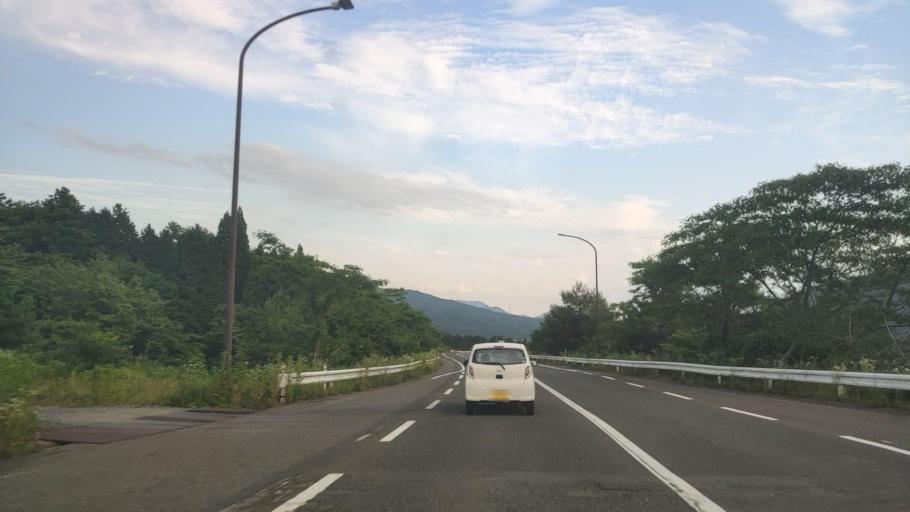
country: JP
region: Tottori
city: Kurayoshi
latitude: 35.2953
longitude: 133.7361
